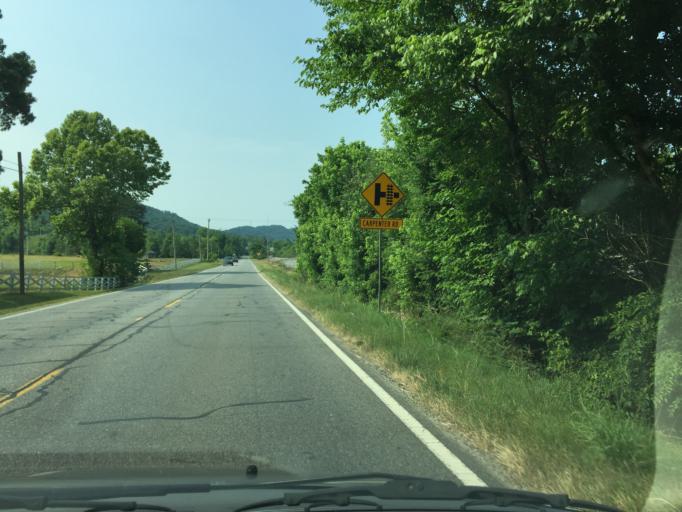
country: US
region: Georgia
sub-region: Catoosa County
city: Ringgold
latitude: 34.9338
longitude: -85.1039
